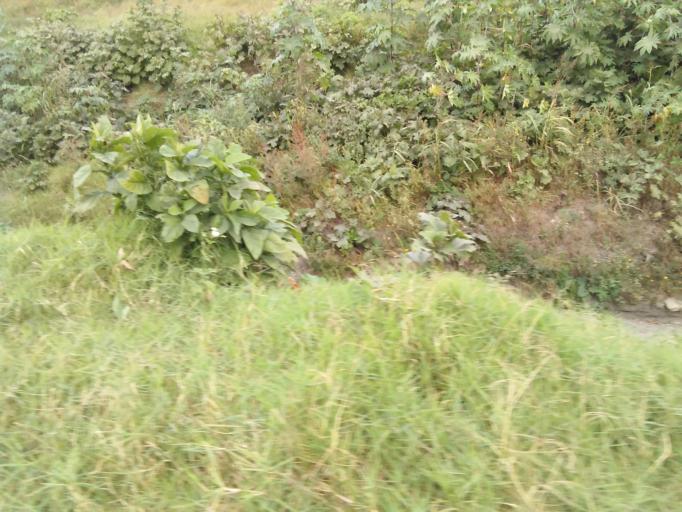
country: MX
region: Nayarit
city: Tepic
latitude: 21.5174
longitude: -104.9130
